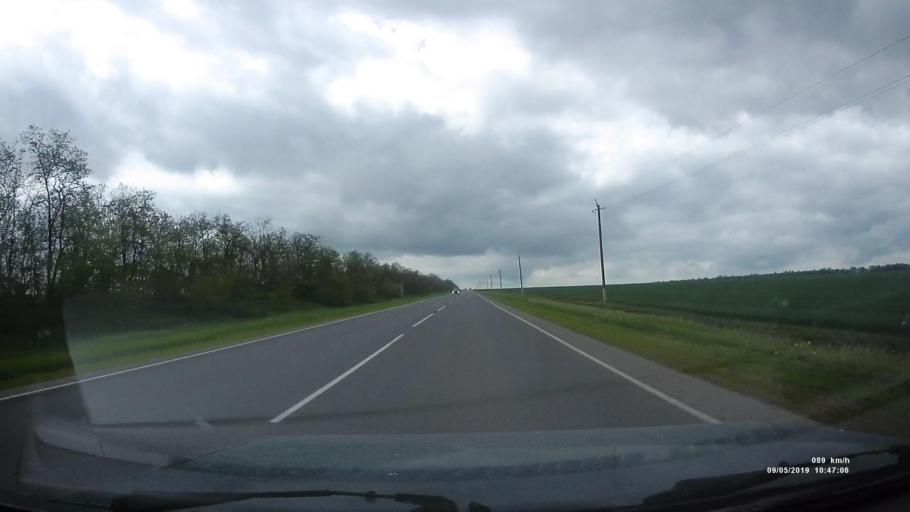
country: RU
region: Rostov
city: Peshkovo
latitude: 46.9755
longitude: 39.3557
